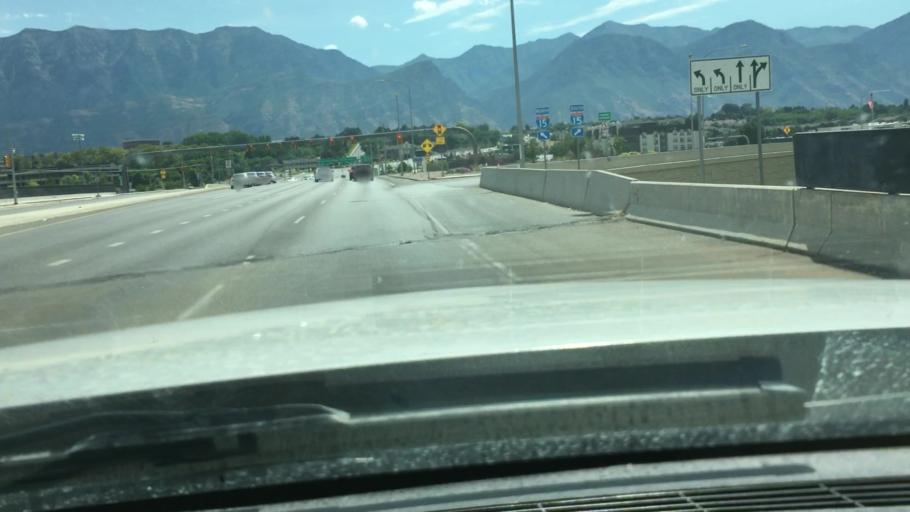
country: US
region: Utah
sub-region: Utah County
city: Orem
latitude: 40.2749
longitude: -111.7211
